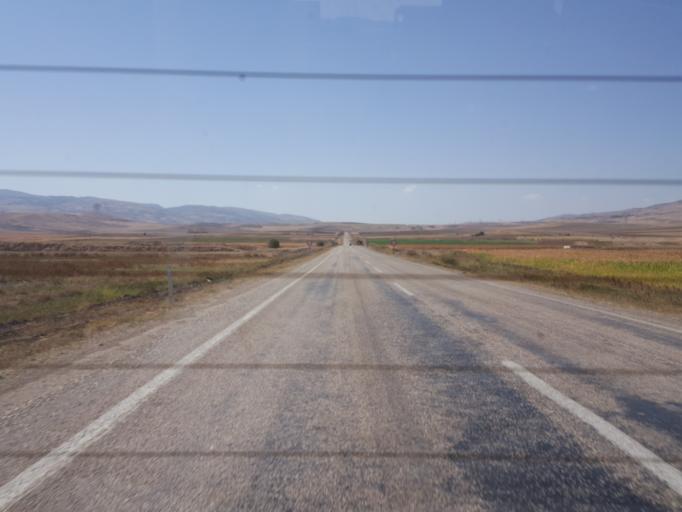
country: TR
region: Amasya
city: Dogantepe
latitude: 40.5765
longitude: 35.6096
